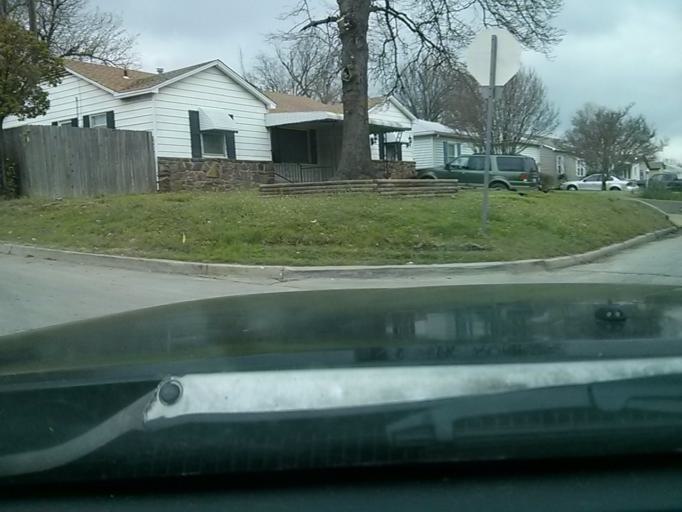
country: US
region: Oklahoma
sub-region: Tulsa County
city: Tulsa
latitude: 36.1662
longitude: -95.9133
